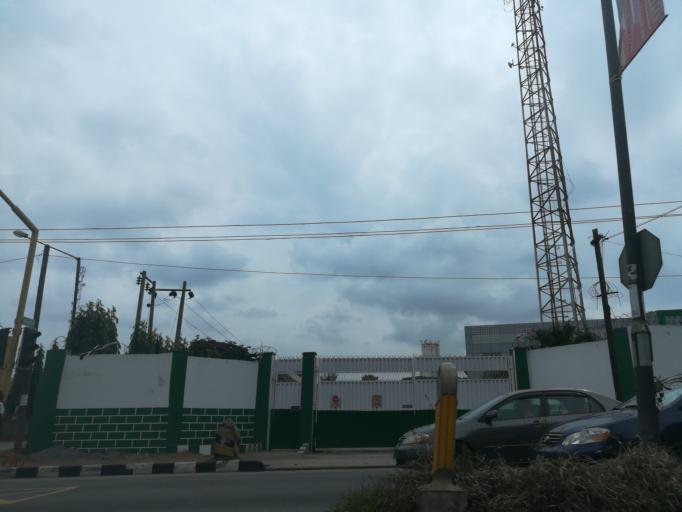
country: NG
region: Lagos
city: Ikeja
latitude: 6.6059
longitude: 3.3602
